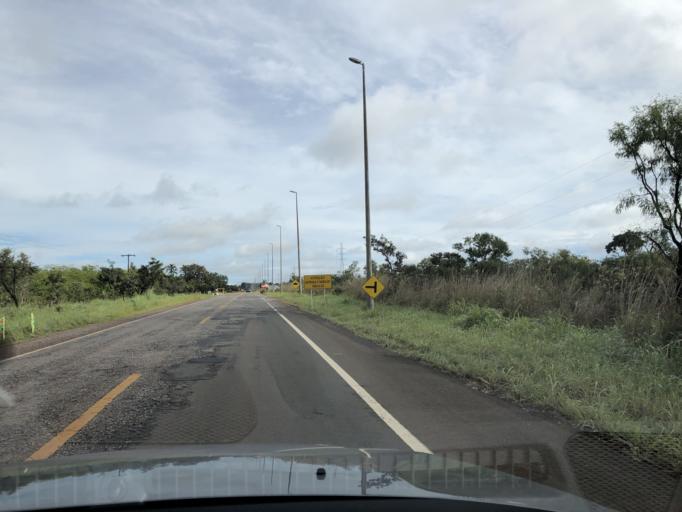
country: BR
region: Federal District
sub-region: Brasilia
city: Brasilia
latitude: -15.6992
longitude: -48.0883
